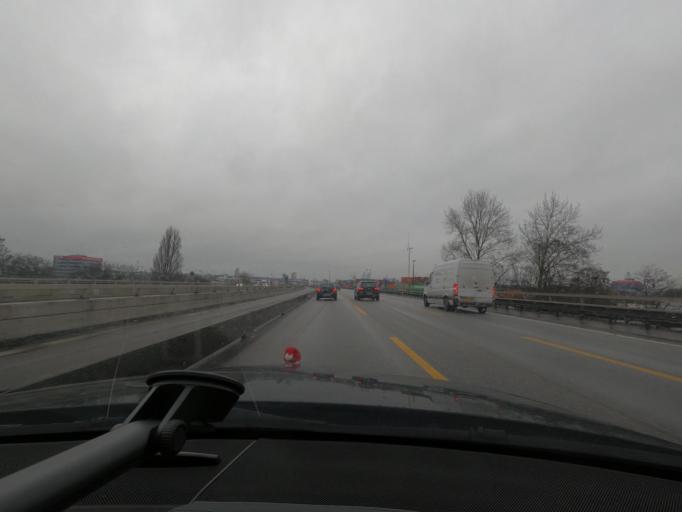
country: DE
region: Hamburg
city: Altona
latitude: 53.5257
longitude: 9.9310
